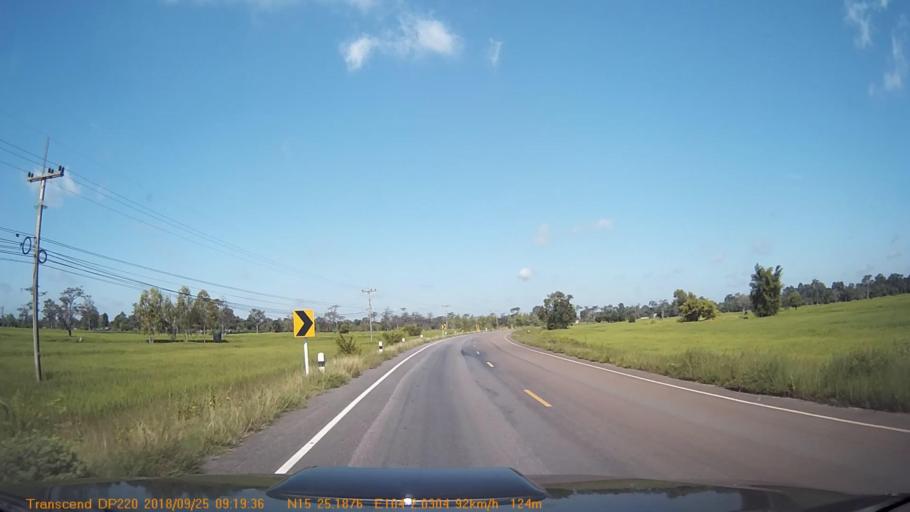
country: TH
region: Sisaket
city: Sila Lat
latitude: 15.4198
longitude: 104.0340
